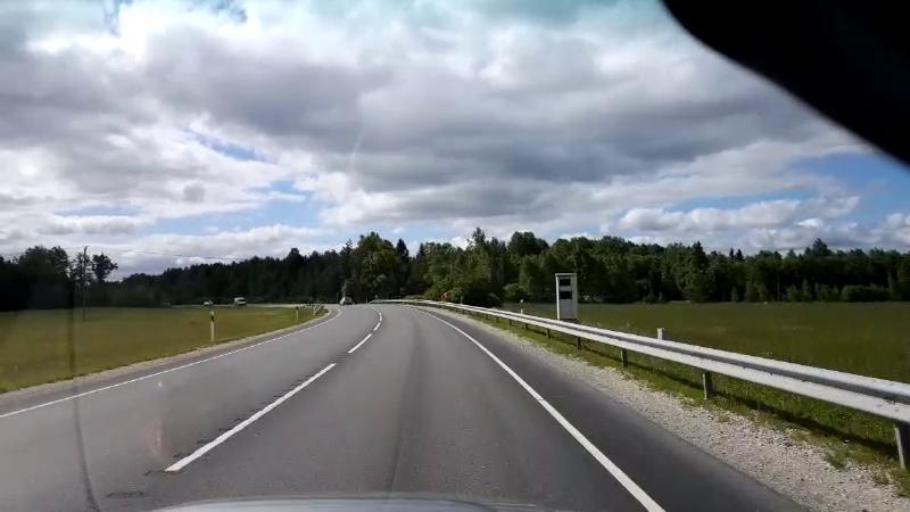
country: EE
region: Paernumaa
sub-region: Halinga vald
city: Parnu-Jaagupi
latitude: 58.6736
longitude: 24.4449
